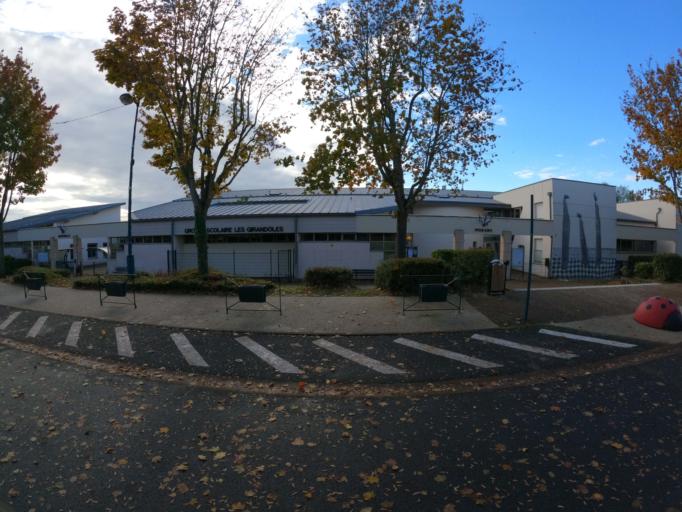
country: FR
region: Ile-de-France
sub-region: Departement de Seine-et-Marne
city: Bailly-Romainvilliers
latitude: 48.8460
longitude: 2.8173
